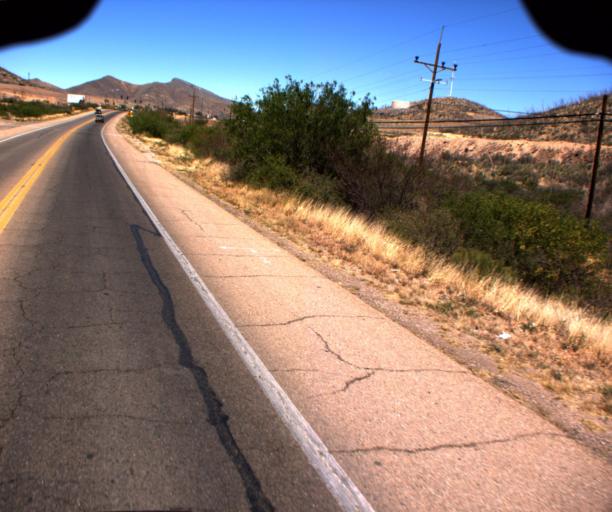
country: US
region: Arizona
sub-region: Cochise County
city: Bisbee
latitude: 31.4105
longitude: -109.9010
